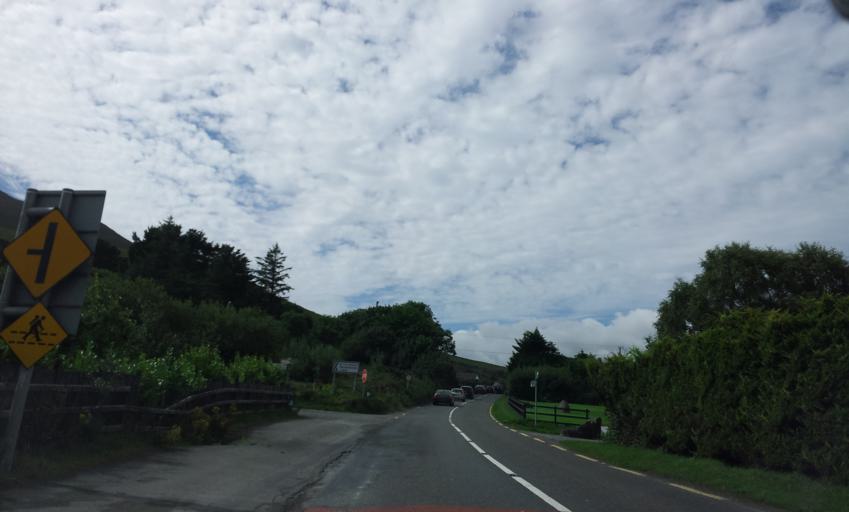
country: IE
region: Munster
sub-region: Ciarrai
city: Killorglin
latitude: 52.0646
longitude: -9.9121
